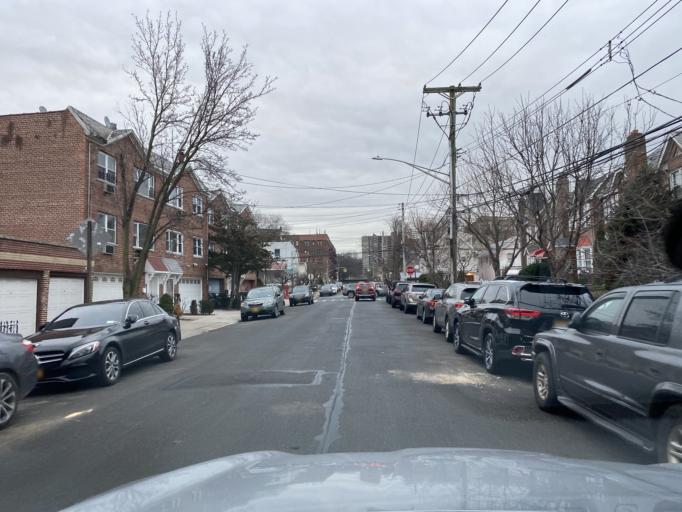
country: US
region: New York
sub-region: New York County
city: Inwood
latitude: 40.8832
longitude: -73.9056
